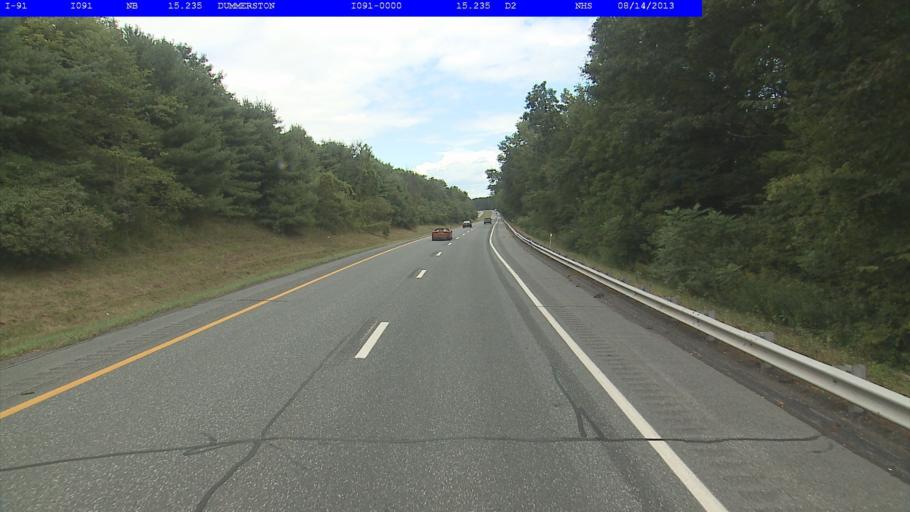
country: US
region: New Hampshire
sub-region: Cheshire County
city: Chesterfield
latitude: 42.9295
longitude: -72.5282
